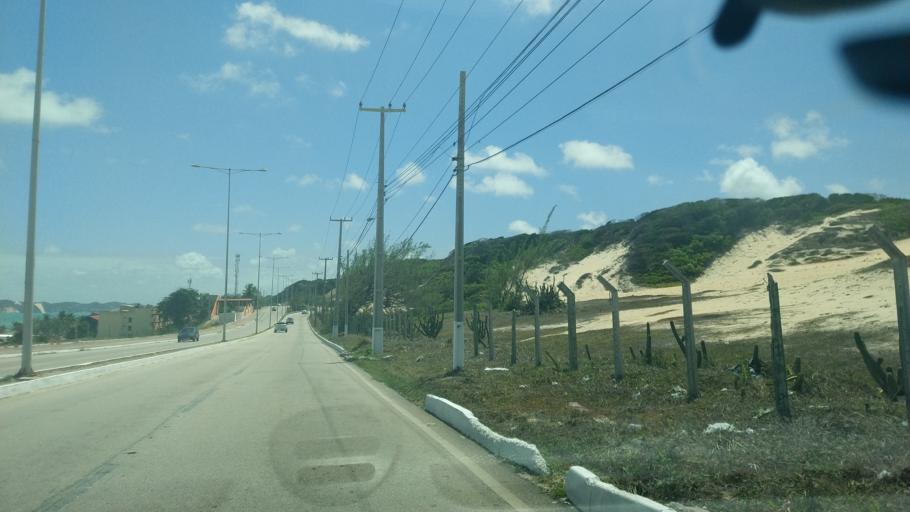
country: BR
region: Rio Grande do Norte
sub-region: Natal
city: Natal
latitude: -5.8240
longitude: -35.1832
